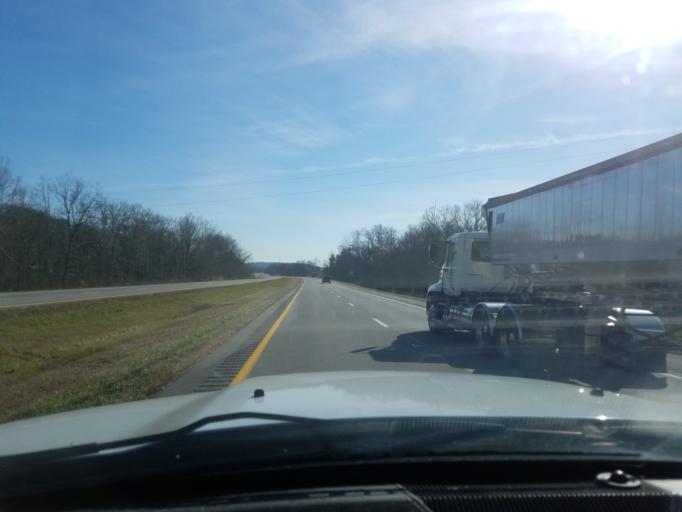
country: US
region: Ohio
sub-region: Pike County
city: Piketon
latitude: 39.0549
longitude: -83.0648
